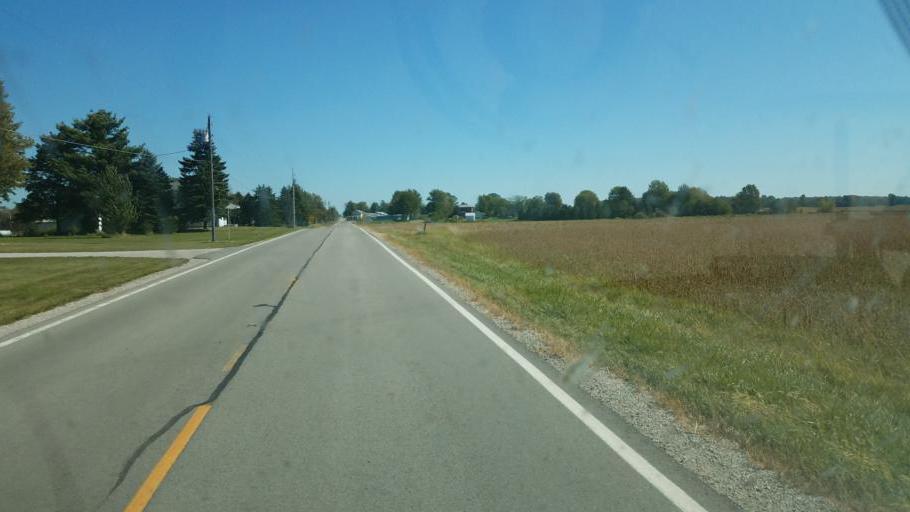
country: US
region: Ohio
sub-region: Crawford County
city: Bucyrus
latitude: 40.9503
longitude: -82.9501
